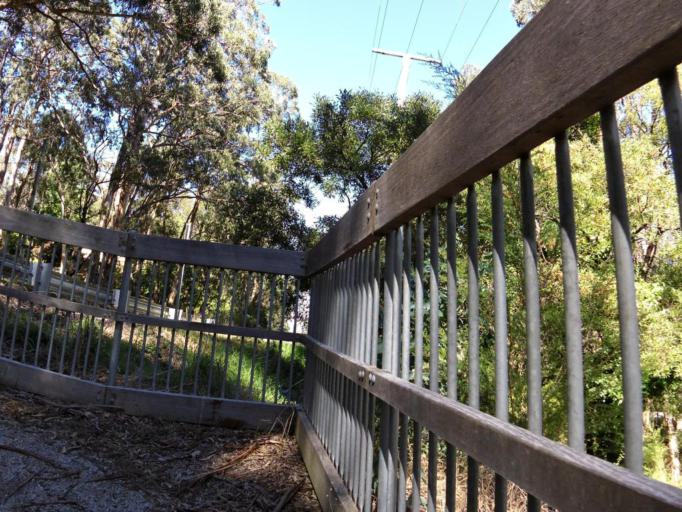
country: AU
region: Victoria
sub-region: Yarra Ranges
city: Yarra Junction
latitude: -37.7370
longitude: 145.5932
